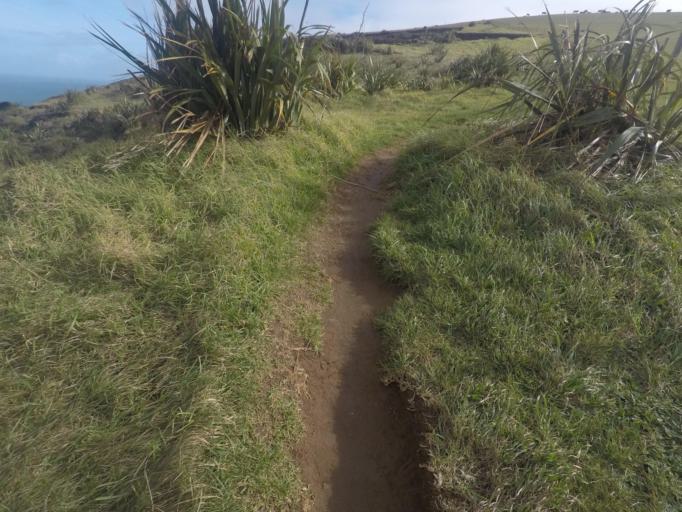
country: NZ
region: Auckland
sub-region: Auckland
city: Muriwai Beach
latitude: -36.8793
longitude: 174.4393
